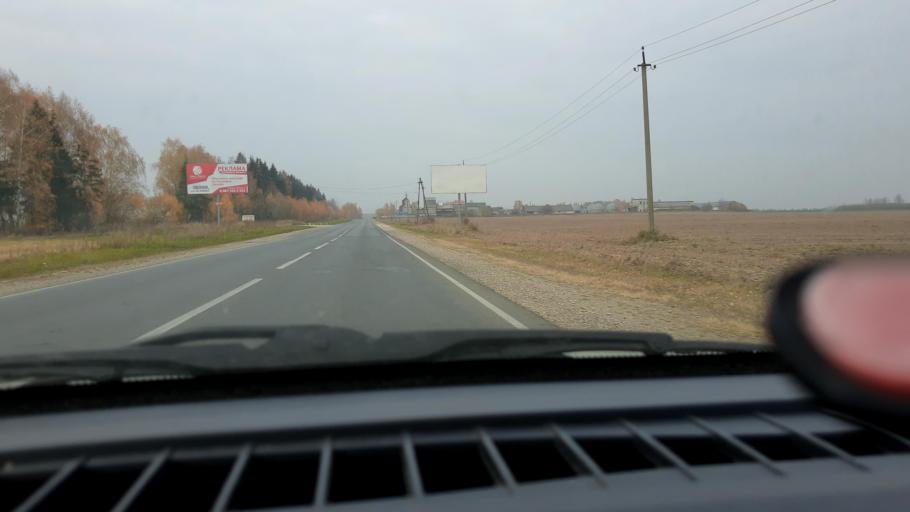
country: RU
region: Nizjnij Novgorod
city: Gorodets
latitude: 56.6326
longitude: 43.5361
